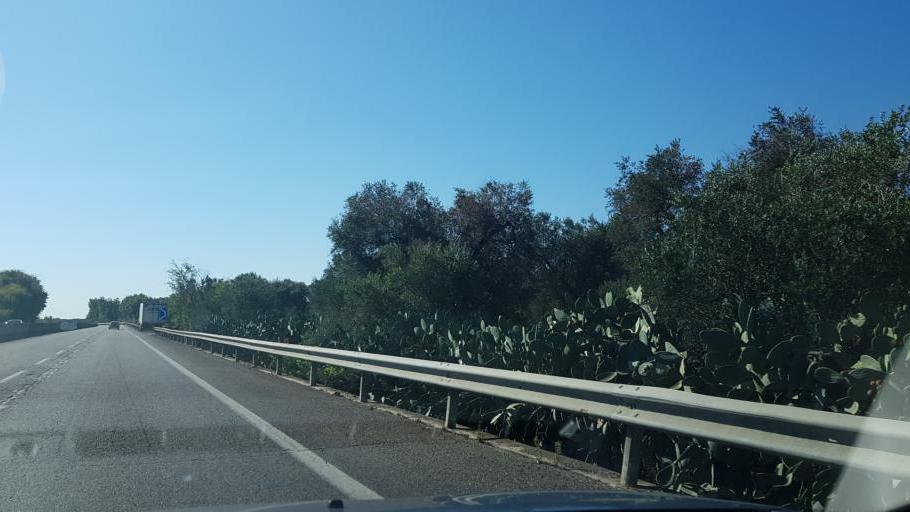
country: IT
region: Apulia
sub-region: Provincia di Brindisi
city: San Pietro Vernotico
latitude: 40.5096
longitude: 18.0239
